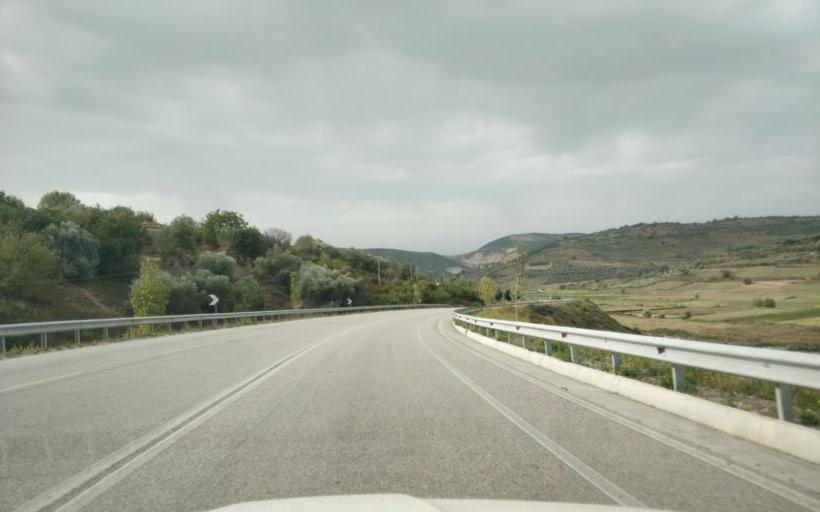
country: AL
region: Fier
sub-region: Rrethi i Mallakastres
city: Fratar
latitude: 40.4927
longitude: 19.8312
